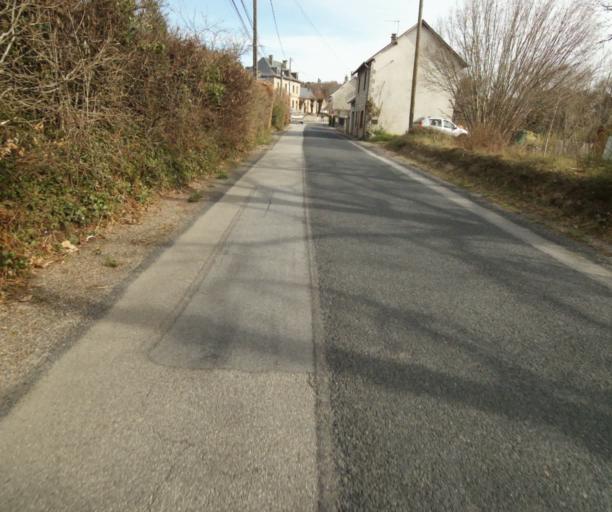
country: FR
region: Limousin
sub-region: Departement de la Correze
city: Correze
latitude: 45.4234
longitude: 1.8331
